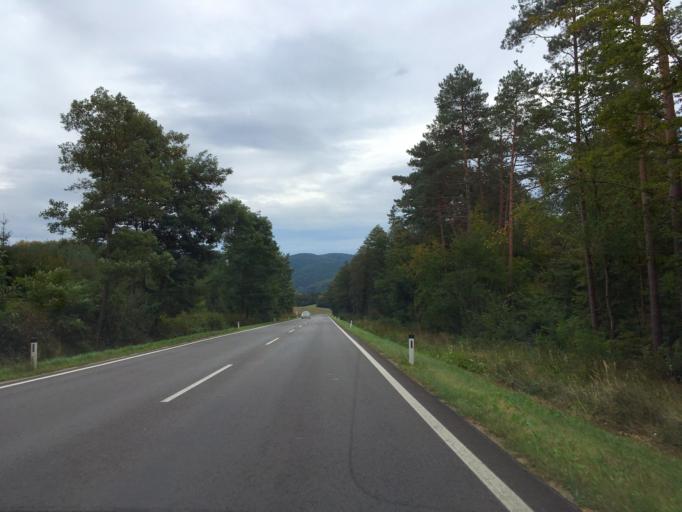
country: AT
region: Lower Austria
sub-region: Politischer Bezirk Modling
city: Gaaden
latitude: 48.0536
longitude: 16.1823
